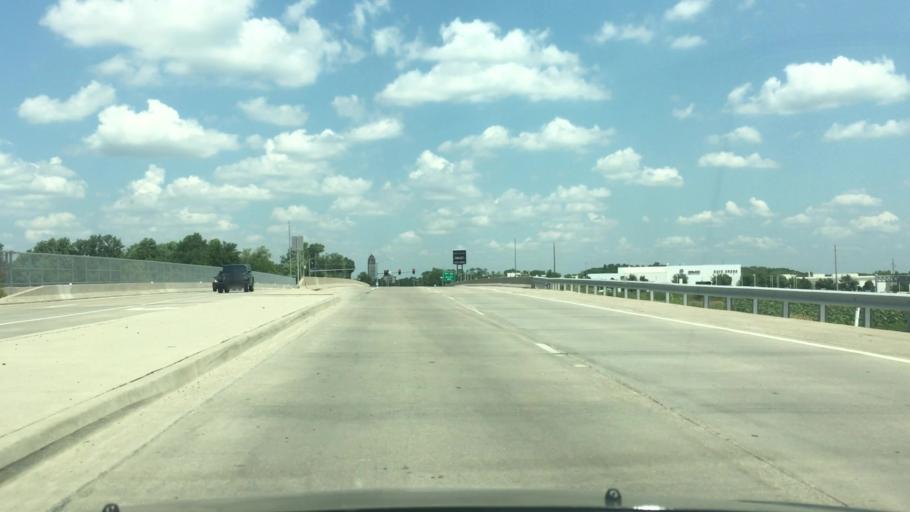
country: US
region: Missouri
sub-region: Jackson County
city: Lees Summit
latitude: 38.9355
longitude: -94.4022
